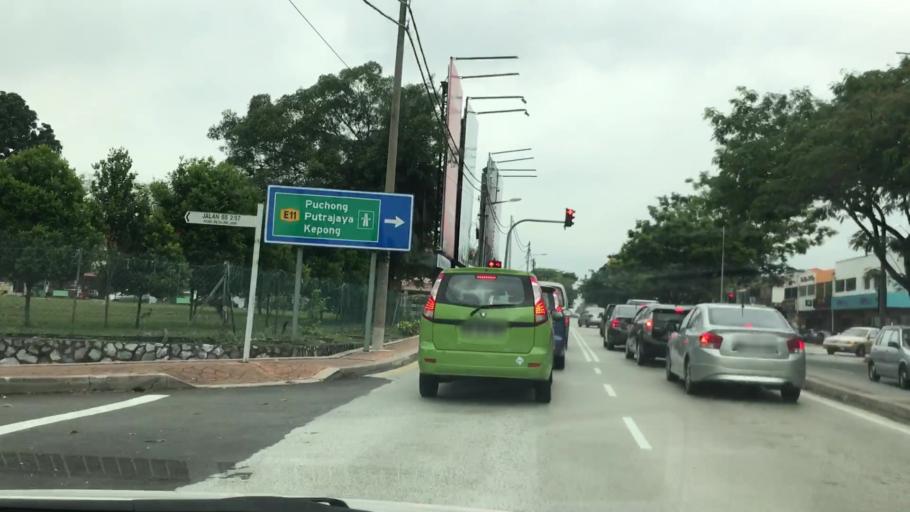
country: MY
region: Selangor
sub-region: Petaling
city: Petaling Jaya
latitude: 3.1163
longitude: 101.6227
